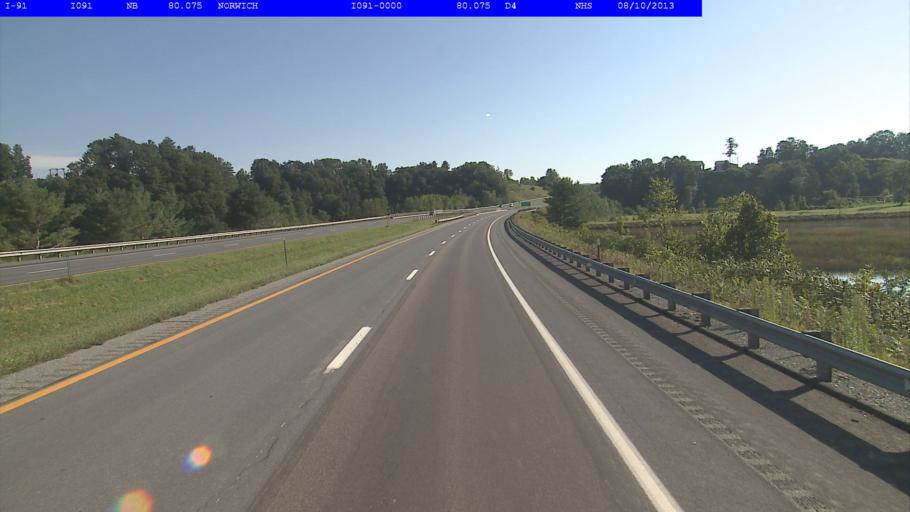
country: US
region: New Hampshire
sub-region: Grafton County
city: Hanover
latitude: 43.7585
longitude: -72.2346
